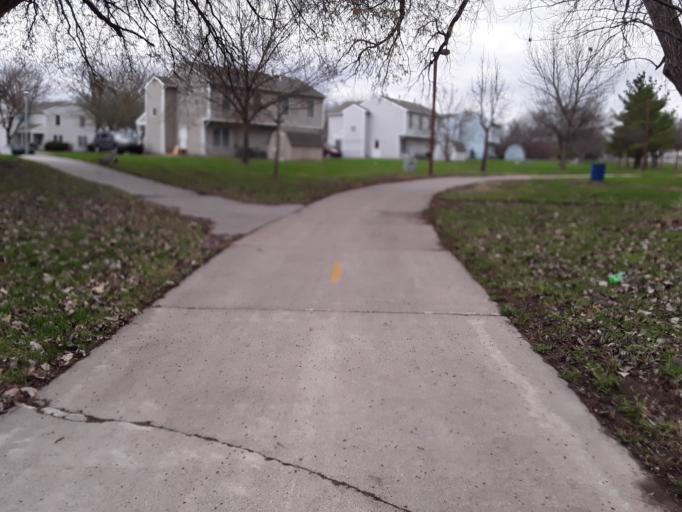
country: US
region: Nebraska
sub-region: Lancaster County
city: Lincoln
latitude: 40.8315
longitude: -96.6867
